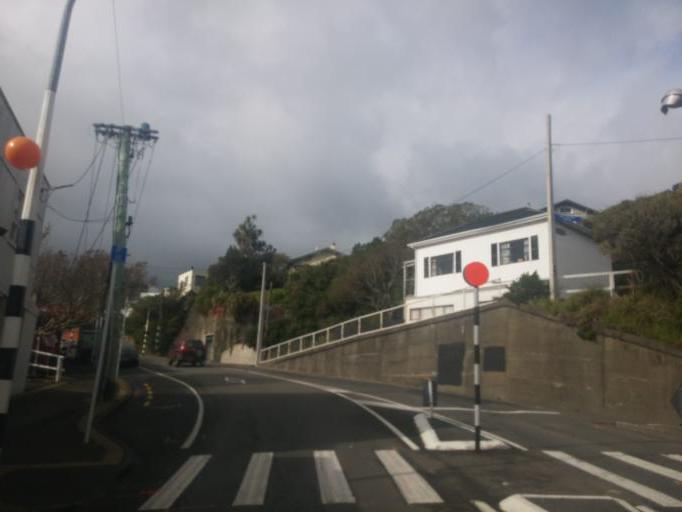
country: NZ
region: Wellington
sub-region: Wellington City
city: Kelburn
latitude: -41.2619
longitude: 174.7740
